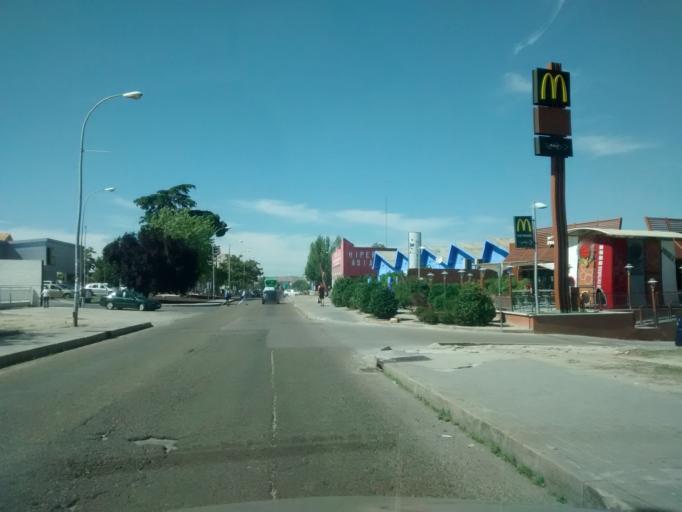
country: ES
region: Madrid
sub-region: Provincia de Madrid
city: San Fernando de Henares
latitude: 40.4309
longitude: -3.5334
